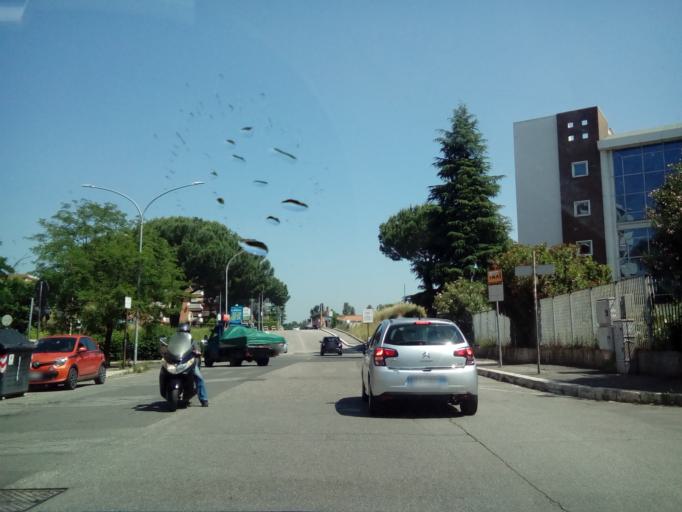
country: IT
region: Latium
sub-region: Citta metropolitana di Roma Capitale
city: Rome
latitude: 41.8897
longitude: 12.5873
